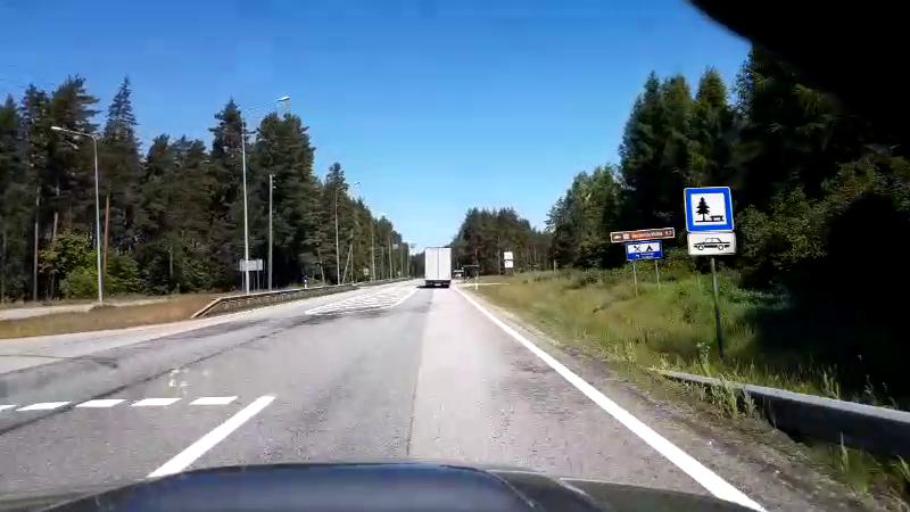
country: LV
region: Salacgrivas
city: Salacgriva
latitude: 57.5725
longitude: 24.4343
